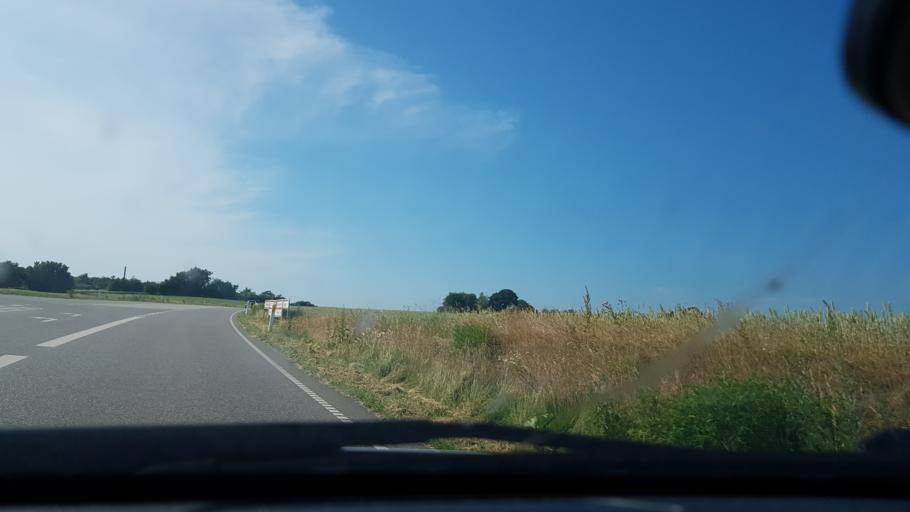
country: DK
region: Zealand
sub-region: Odsherred Kommune
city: Hojby
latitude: 55.8511
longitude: 11.5948
